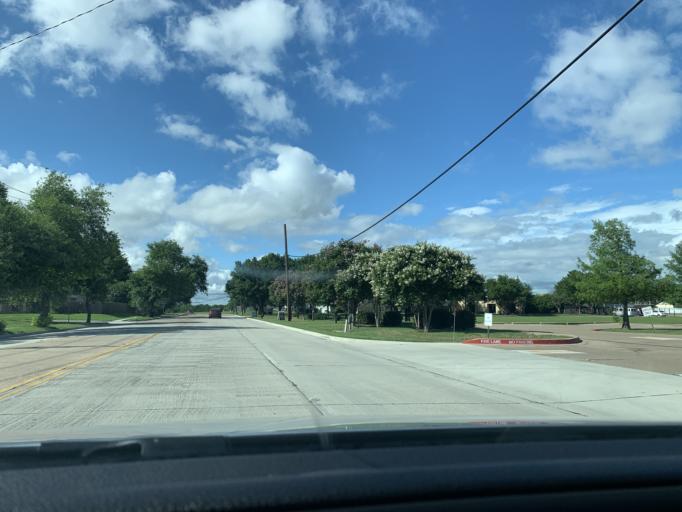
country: US
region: Texas
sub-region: Dallas County
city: Grand Prairie
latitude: 32.6599
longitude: -97.0278
